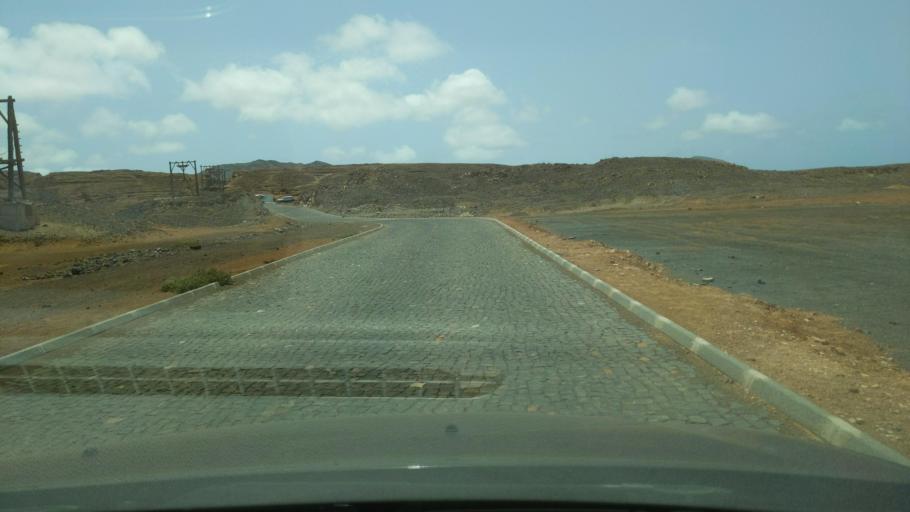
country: CV
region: Sal
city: Espargos
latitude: 16.7669
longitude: -22.8947
